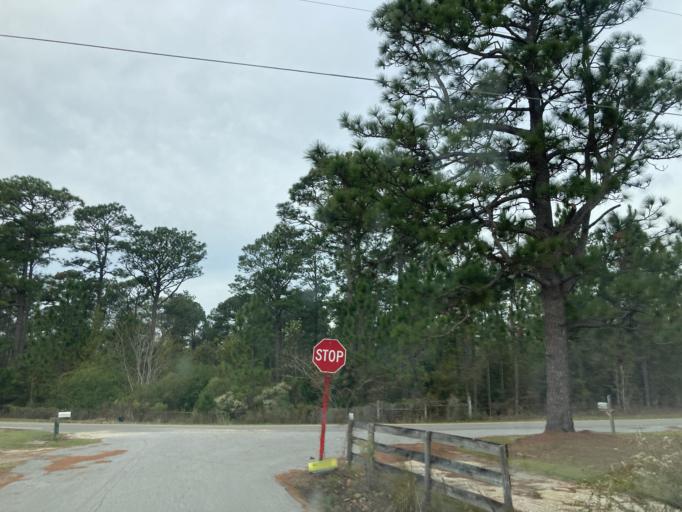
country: US
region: Mississippi
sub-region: Lamar County
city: Purvis
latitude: 31.1596
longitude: -89.4604
